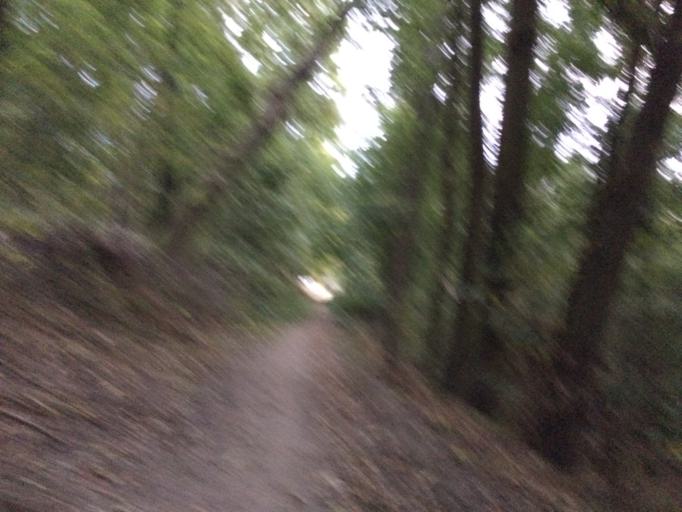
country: FR
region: Ile-de-France
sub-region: Departement des Yvelines
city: Velizy-Villacoublay
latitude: 48.7634
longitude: 2.1945
